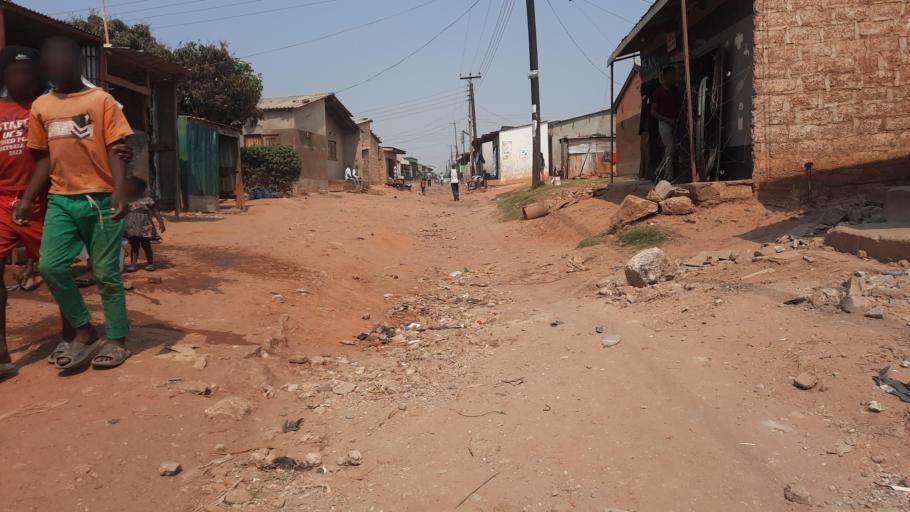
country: ZM
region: Lusaka
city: Lusaka
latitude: -15.4048
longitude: 28.3777
